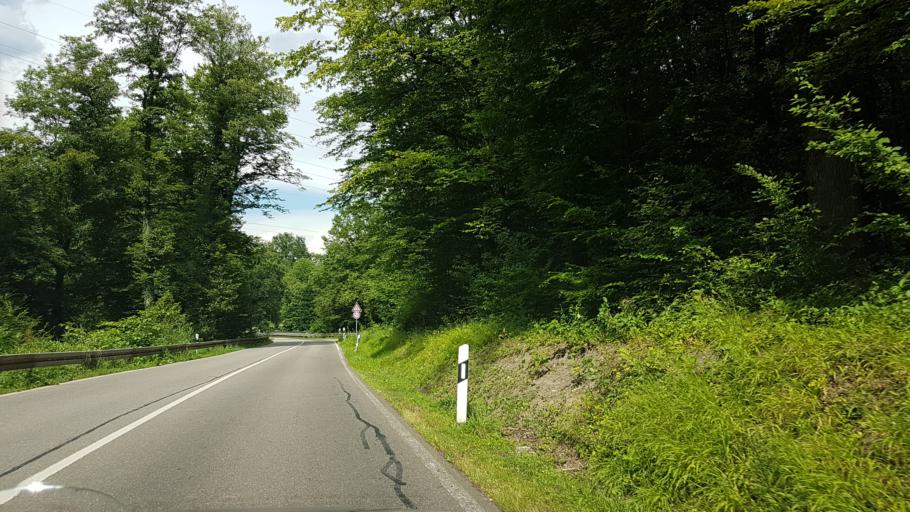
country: DE
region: Saarland
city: Saarbrucken
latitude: 49.2639
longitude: 6.9815
